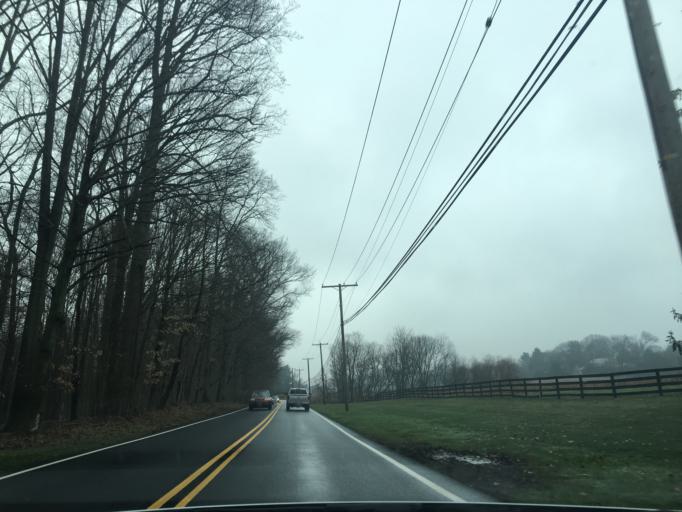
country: US
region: Maryland
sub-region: Baltimore County
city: Garrison
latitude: 39.3915
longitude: -76.7723
